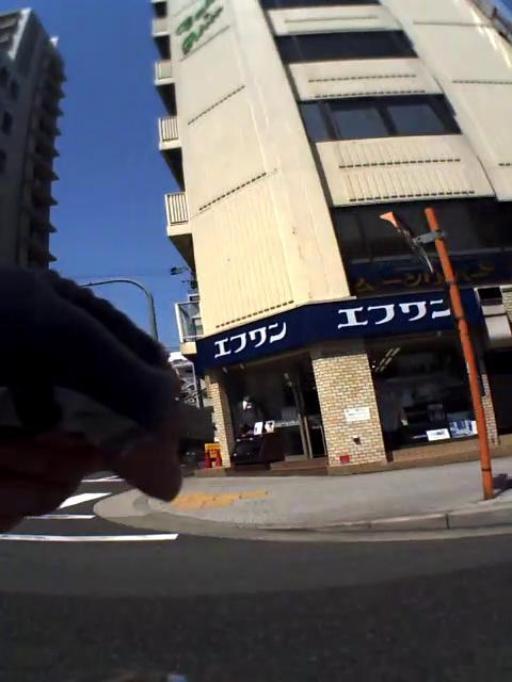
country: JP
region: Osaka
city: Osaka-shi
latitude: 34.6881
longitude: 135.5173
